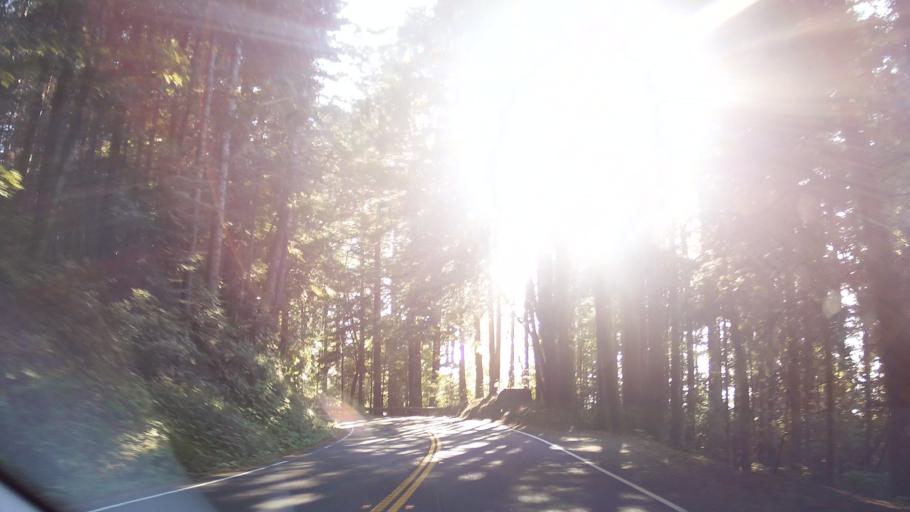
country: US
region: California
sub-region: Mendocino County
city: Fort Bragg
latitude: 39.3590
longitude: -123.6233
